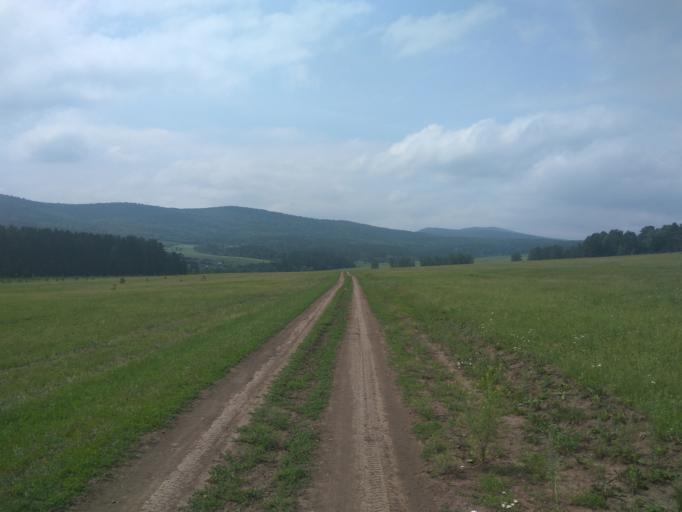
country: RU
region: Krasnoyarskiy
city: Zykovo
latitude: 55.8461
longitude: 93.2079
